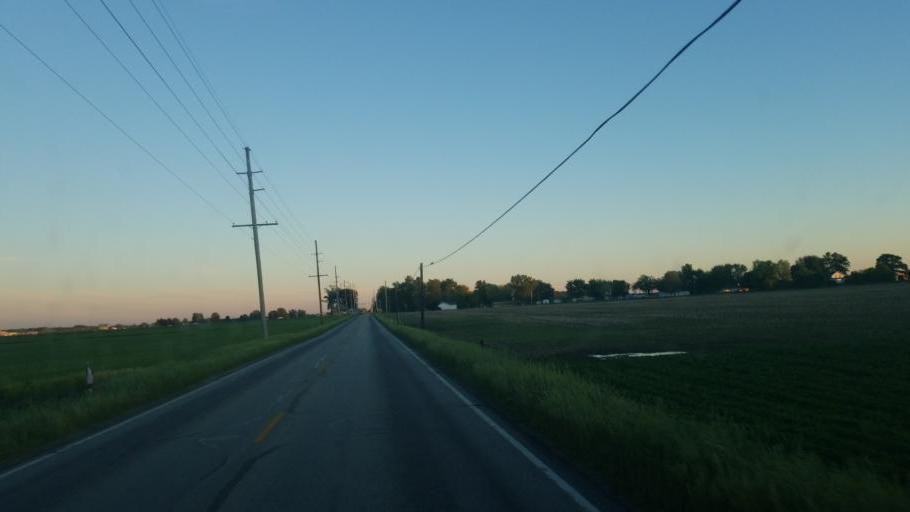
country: US
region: Indiana
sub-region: Elkhart County
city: Nappanee
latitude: 41.3652
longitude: -86.0006
